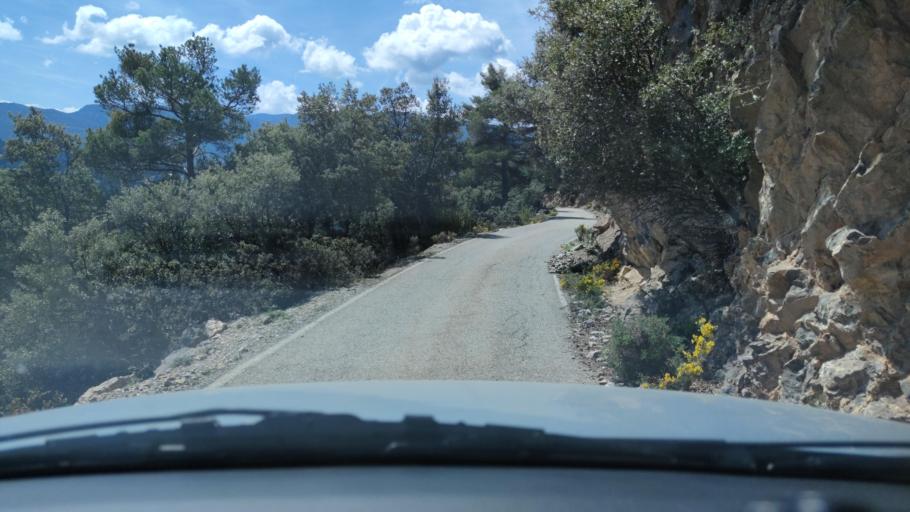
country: ES
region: Catalonia
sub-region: Provincia de Lleida
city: Sort
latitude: 42.3129
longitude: 1.1332
